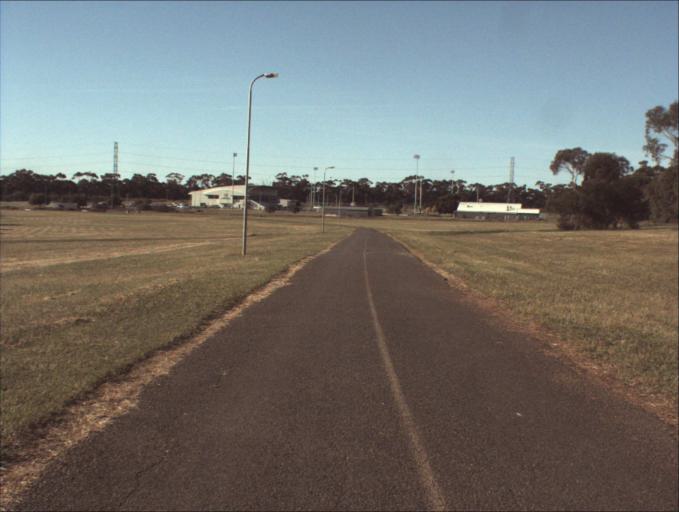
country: AU
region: South Australia
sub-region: Port Adelaide Enfield
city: Enfield
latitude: -34.8426
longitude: 138.6138
